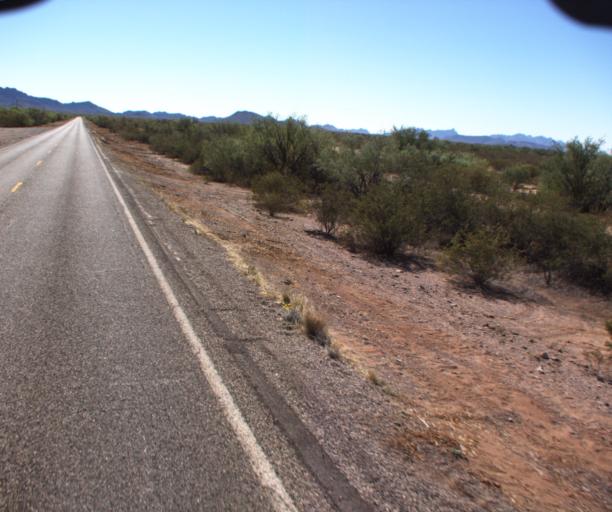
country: US
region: Arizona
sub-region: Pima County
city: Ajo
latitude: 32.3307
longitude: -112.7842
